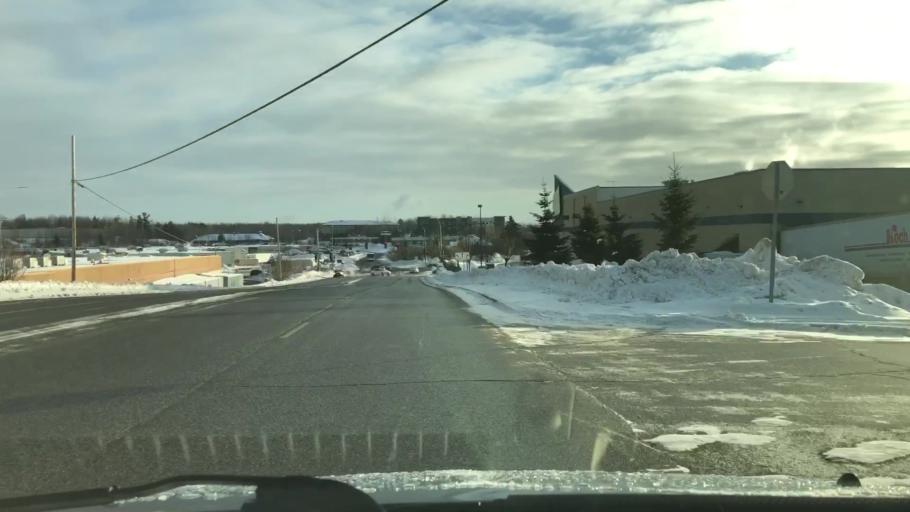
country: US
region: Minnesota
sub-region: Saint Louis County
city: Duluth
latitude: 46.8096
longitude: -92.1694
